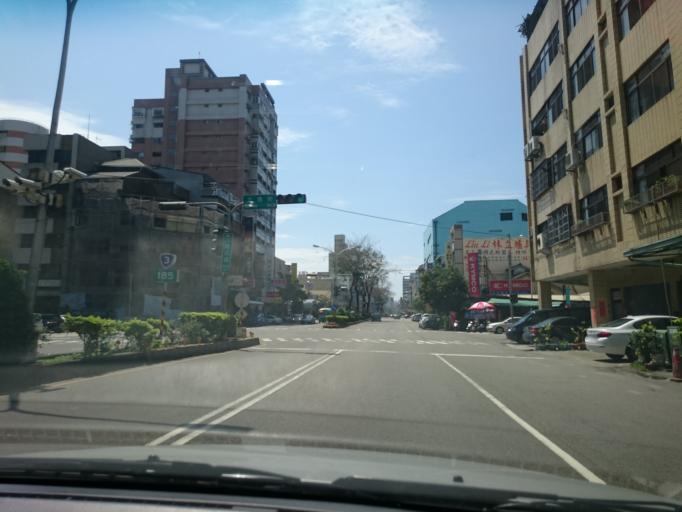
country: TW
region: Taiwan
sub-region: Taichung City
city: Taichung
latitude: 24.1312
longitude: 120.6888
